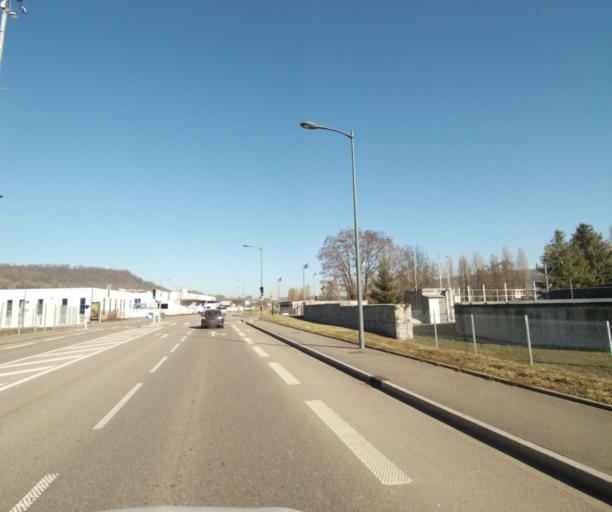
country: FR
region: Lorraine
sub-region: Departement de Meurthe-et-Moselle
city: Maxeville
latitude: 48.7127
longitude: 6.1724
